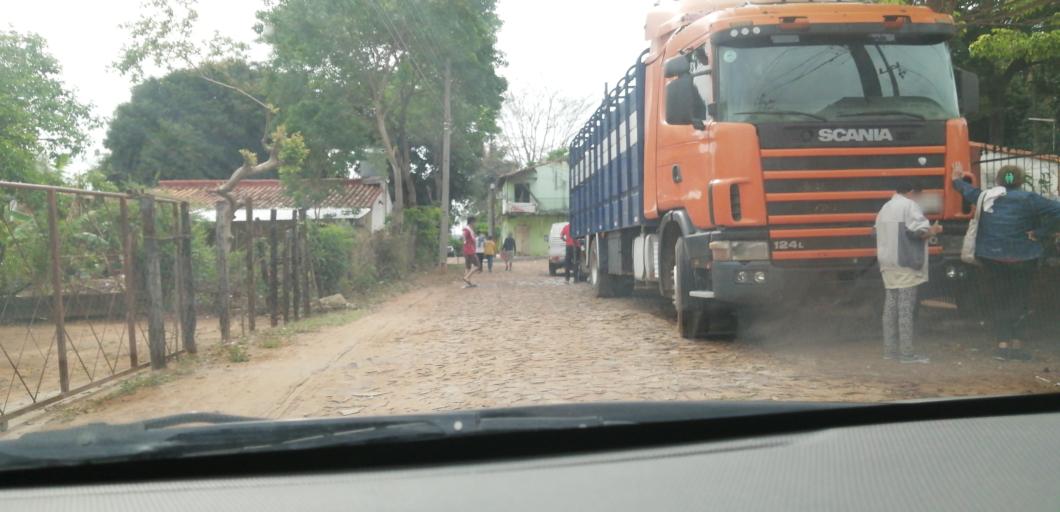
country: PY
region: Central
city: Colonia Mariano Roque Alonso
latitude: -25.1929
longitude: -57.5390
